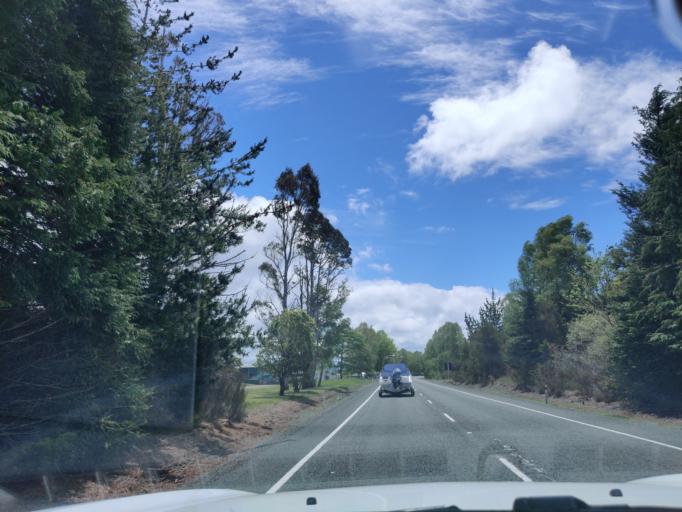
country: NZ
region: Waikato
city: Turangi
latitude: -39.0052
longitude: 175.8049
